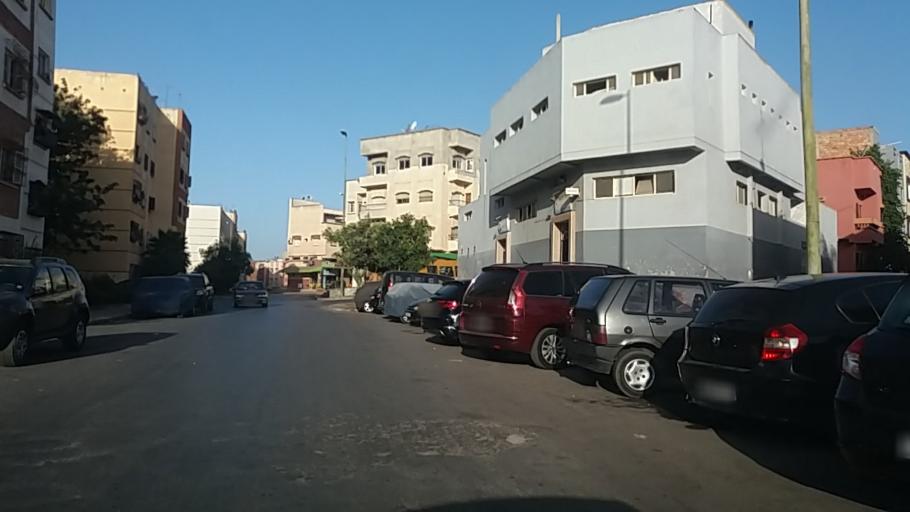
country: MA
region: Gharb-Chrarda-Beni Hssen
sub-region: Kenitra Province
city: Kenitra
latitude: 34.2561
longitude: -6.6210
